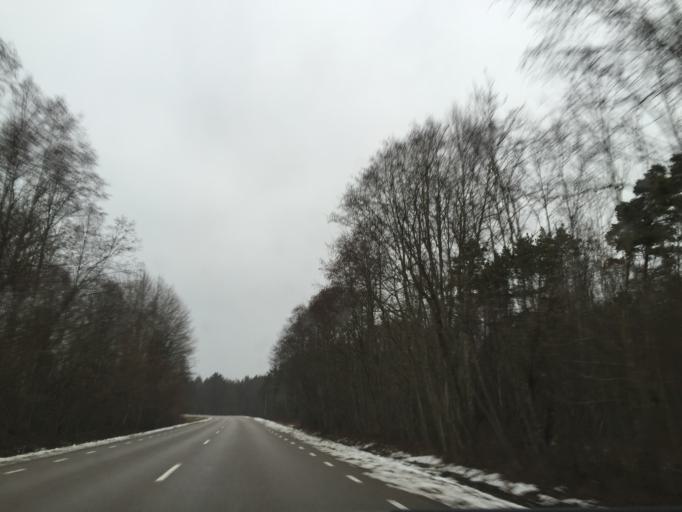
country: EE
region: Saare
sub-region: Kuressaare linn
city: Kuressaare
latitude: 58.3926
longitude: 22.3255
